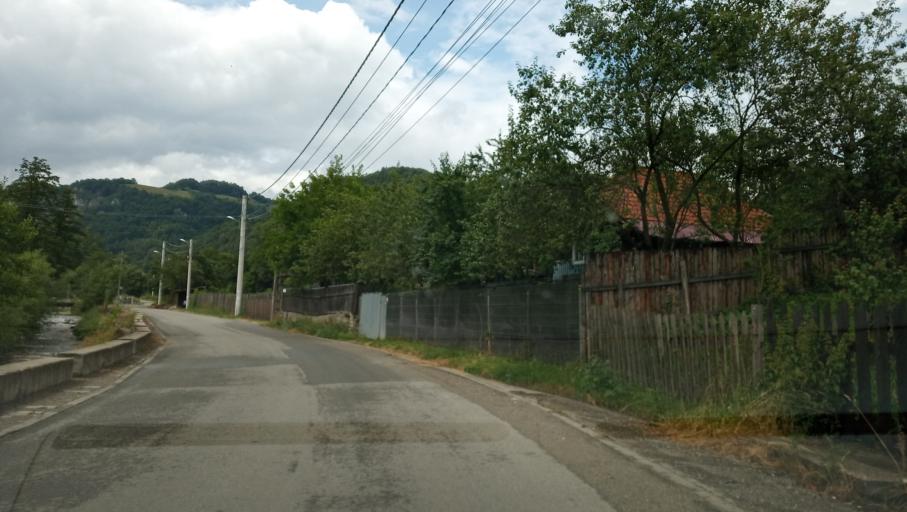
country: RO
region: Hunedoara
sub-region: Oras Petrila
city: Petrila
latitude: 45.4570
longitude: 23.4185
